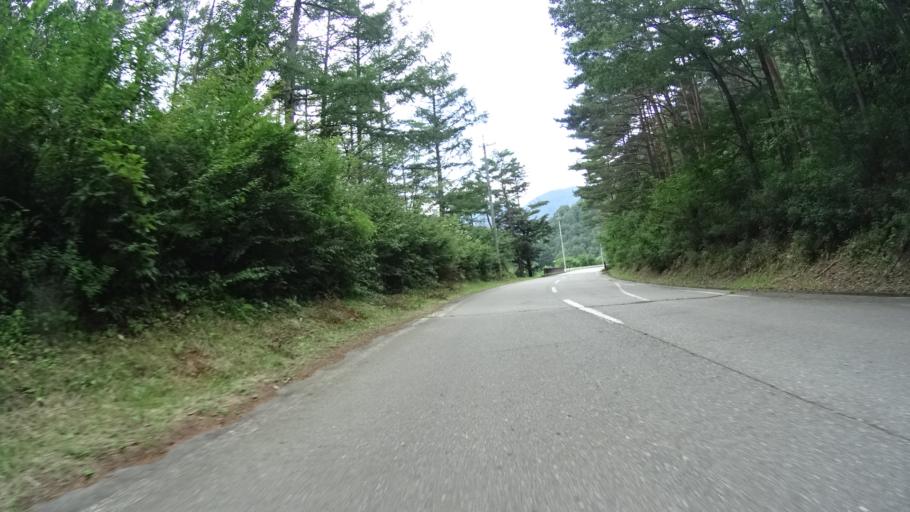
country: JP
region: Nagano
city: Saku
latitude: 36.0701
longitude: 138.6166
